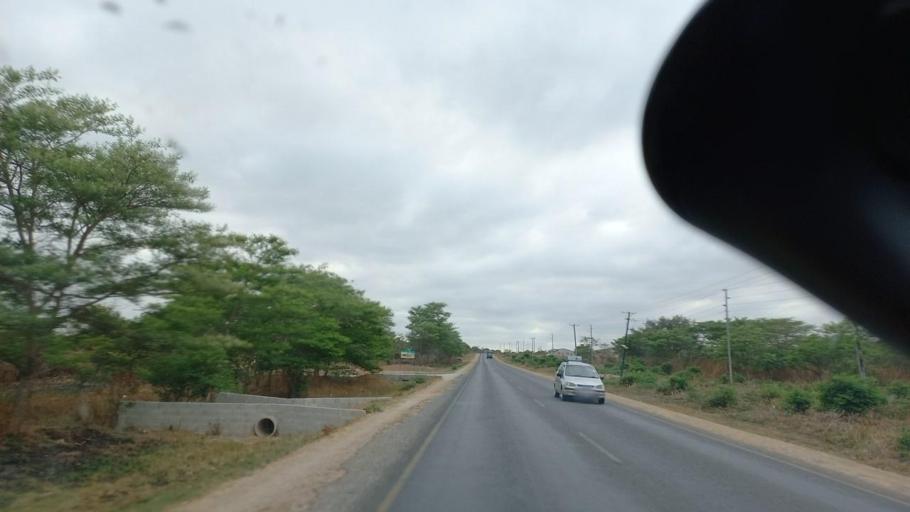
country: ZM
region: Lusaka
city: Chongwe
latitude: -15.3403
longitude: 28.6304
